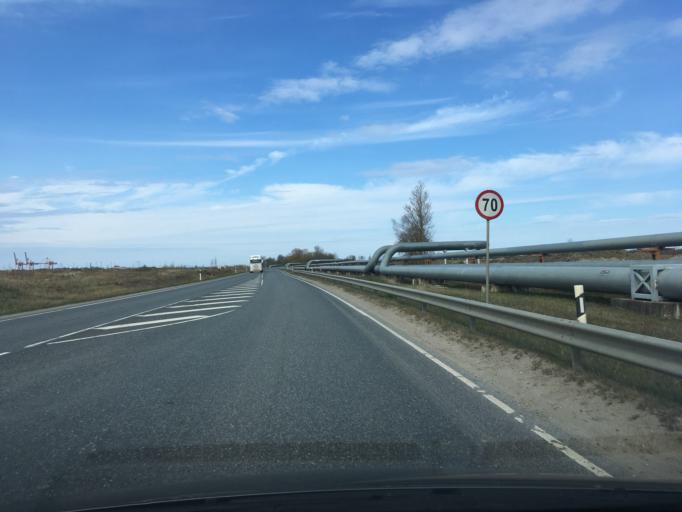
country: EE
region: Harju
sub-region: Maardu linn
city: Maardu
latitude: 59.4693
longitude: 24.9806
